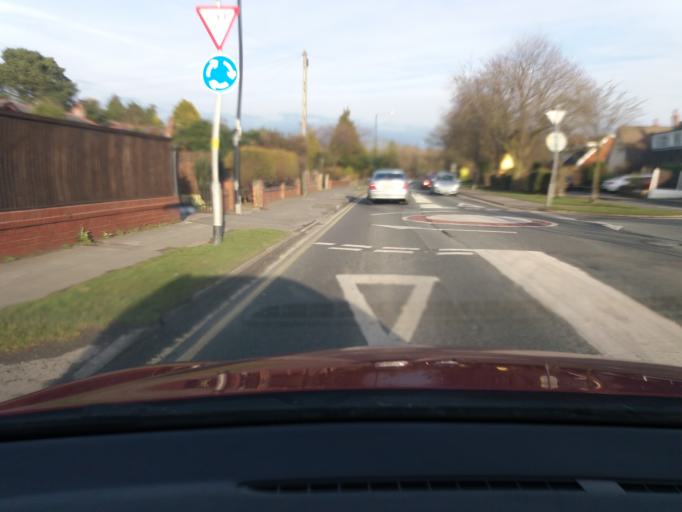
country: GB
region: England
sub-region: Lancashire
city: Euxton
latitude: 53.6607
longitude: -2.6667
